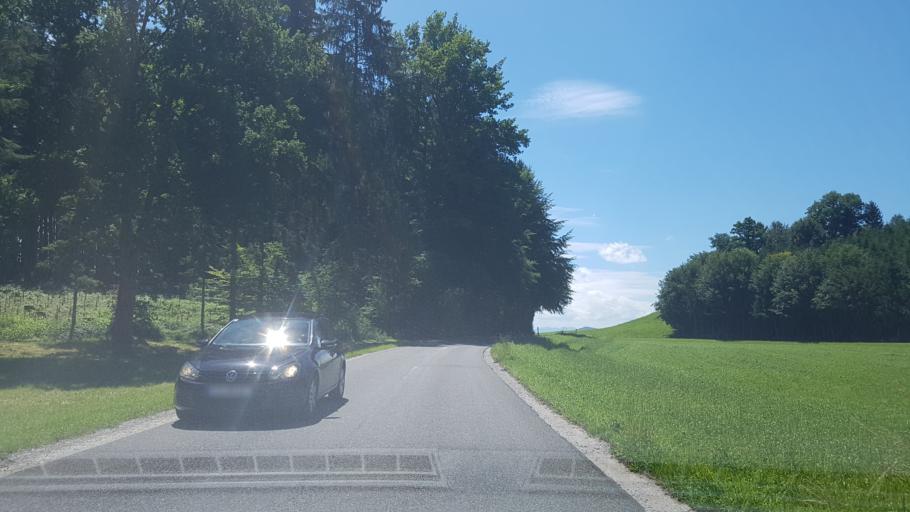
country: AT
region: Salzburg
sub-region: Politischer Bezirk Salzburg-Umgebung
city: Schleedorf
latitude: 48.0020
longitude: 13.1576
